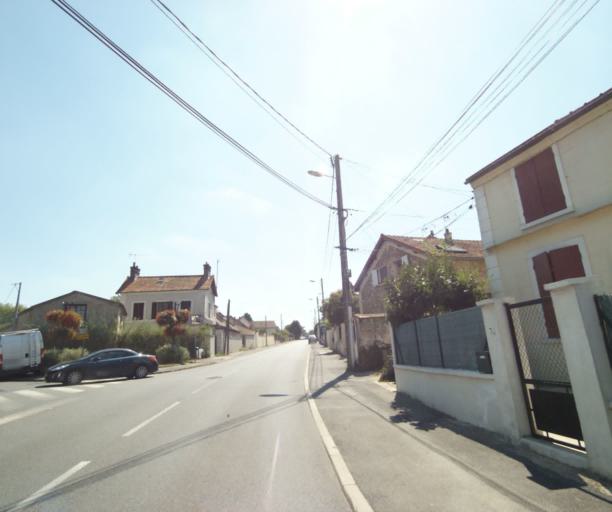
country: FR
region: Ile-de-France
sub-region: Departement de Seine-et-Marne
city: Lagny-sur-Marne
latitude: 48.8709
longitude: 2.7067
